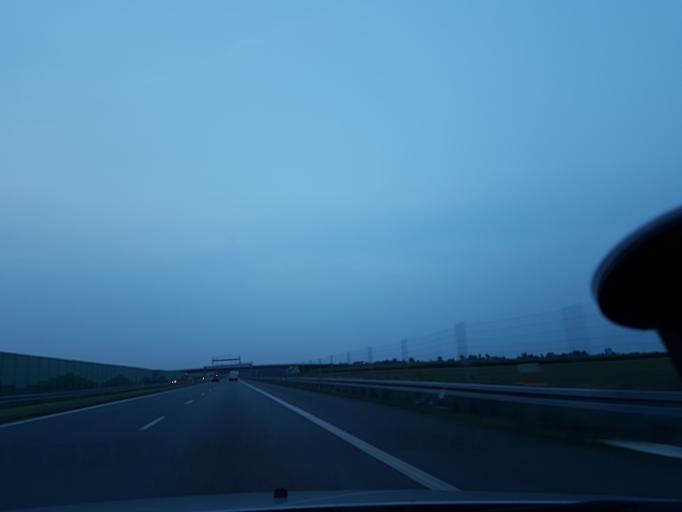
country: PL
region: Lodz Voivodeship
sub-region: Powiat leczycki
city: Piatek
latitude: 52.0868
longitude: 19.5238
